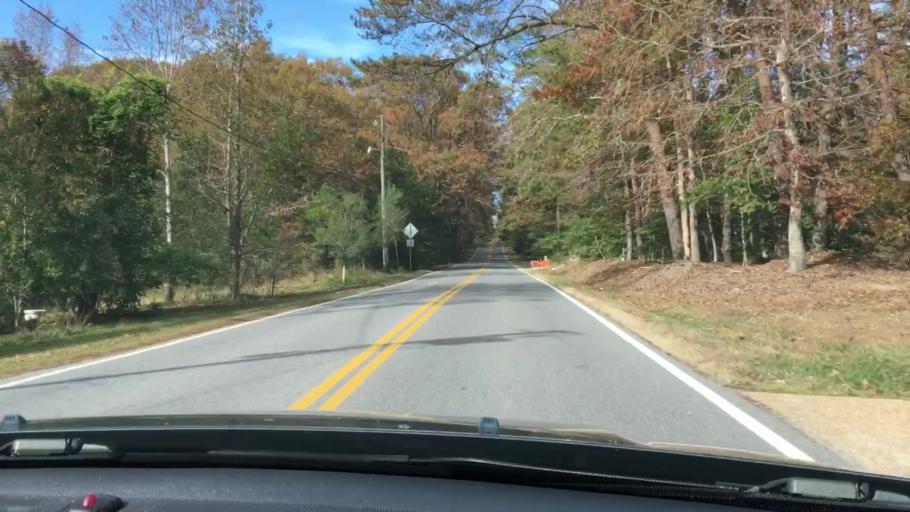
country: US
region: Virginia
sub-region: King William County
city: West Point
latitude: 37.4903
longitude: -76.8129
